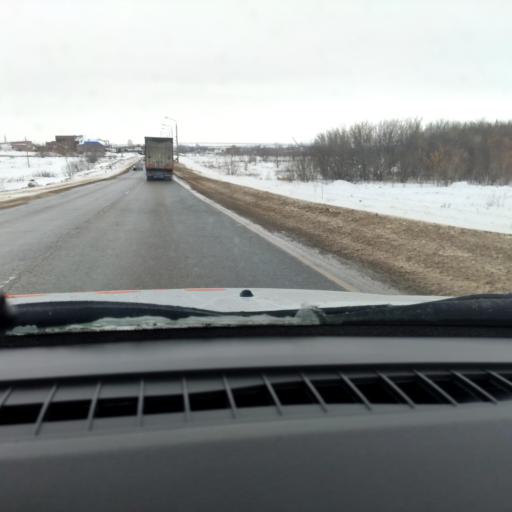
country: RU
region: Samara
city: Dubovyy Umet
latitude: 52.8298
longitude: 50.4951
